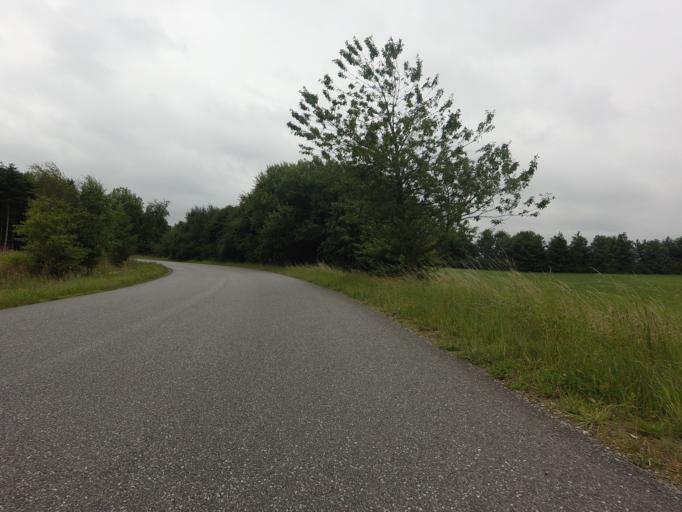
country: DK
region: Central Jutland
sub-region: Horsens Kommune
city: Braedstrup
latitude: 55.9751
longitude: 9.6002
